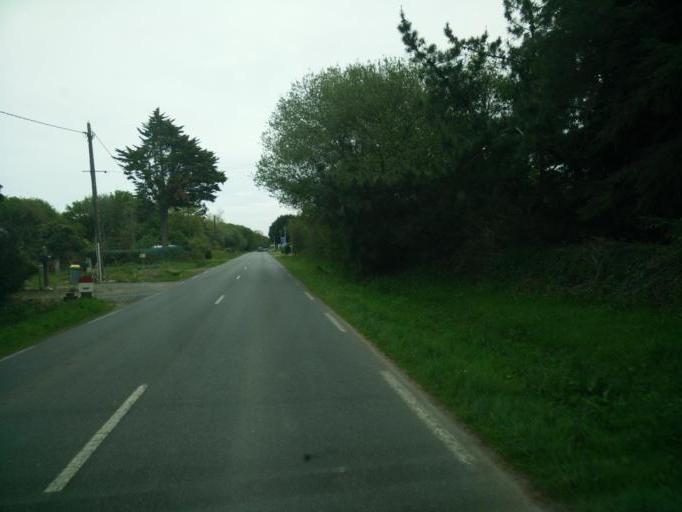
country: FR
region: Brittany
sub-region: Departement des Cotes-d'Armor
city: Pleumeur-Bodou
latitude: 48.7533
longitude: -3.5163
